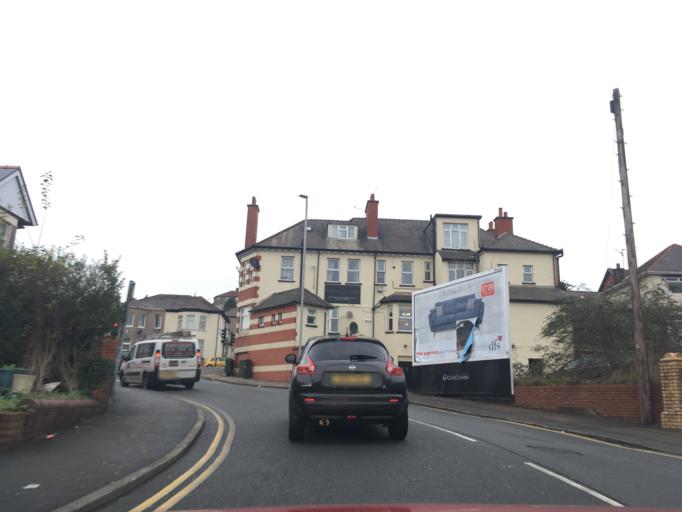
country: GB
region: Wales
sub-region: Newport
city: Caerleon
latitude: 51.5877
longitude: -2.9626
